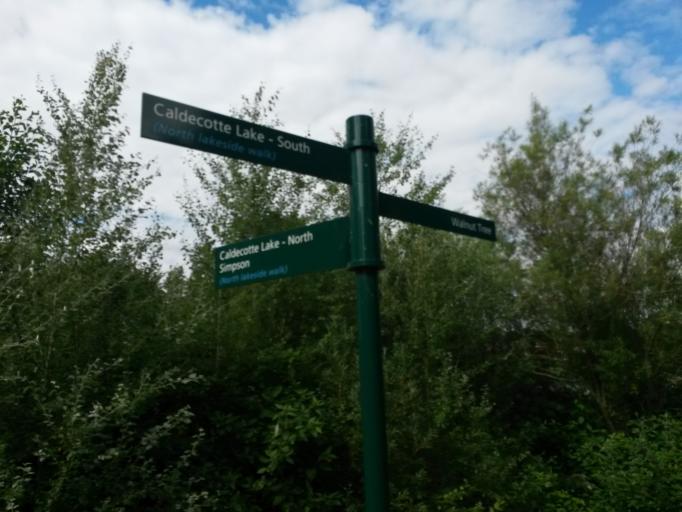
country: GB
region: England
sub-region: Milton Keynes
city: Simpson
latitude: 52.0127
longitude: -0.6994
